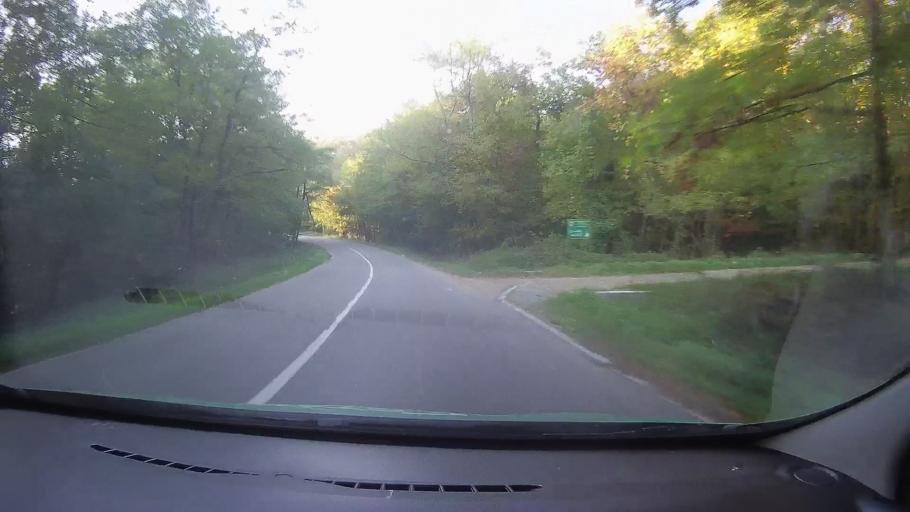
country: RO
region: Timis
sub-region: Comuna Dumbrava
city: Dumbrava
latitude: 45.7572
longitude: 22.1095
